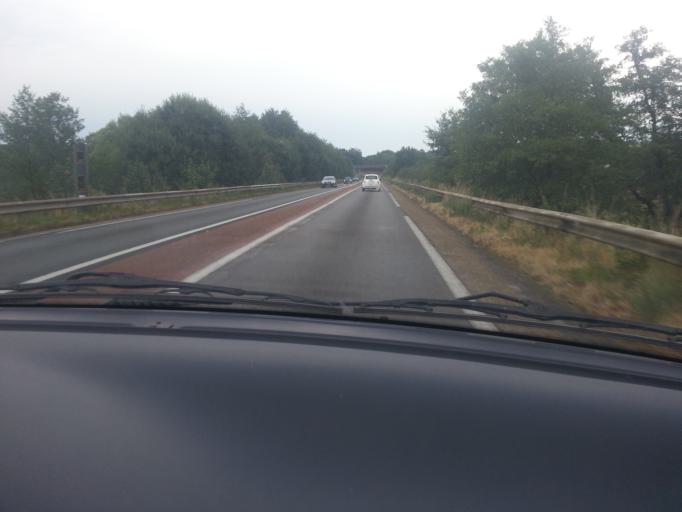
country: FR
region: Bourgogne
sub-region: Departement de Saone-et-Loire
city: Blanzy
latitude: 46.7010
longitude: 4.3963
